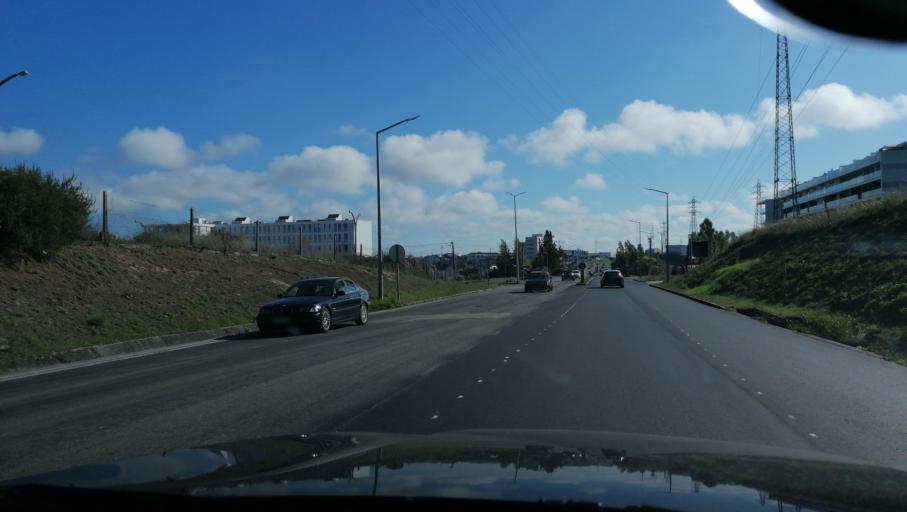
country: PT
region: Aveiro
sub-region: Aveiro
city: Aveiro
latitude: 40.6387
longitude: -8.6334
